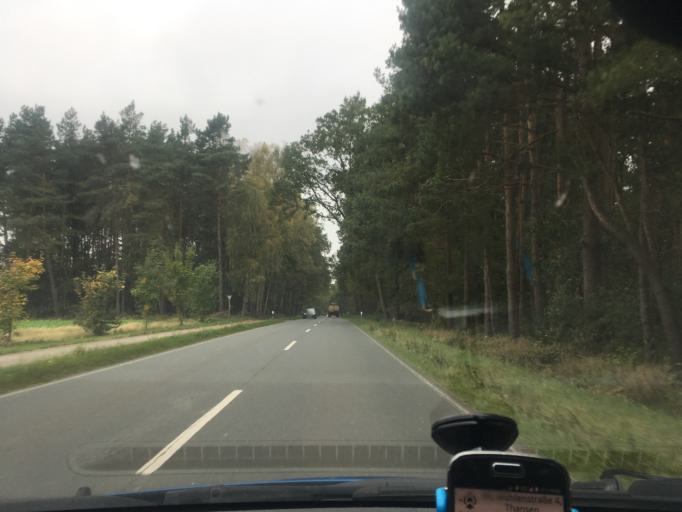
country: DE
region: Lower Saxony
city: Soderstorf
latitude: 53.1342
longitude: 10.1585
